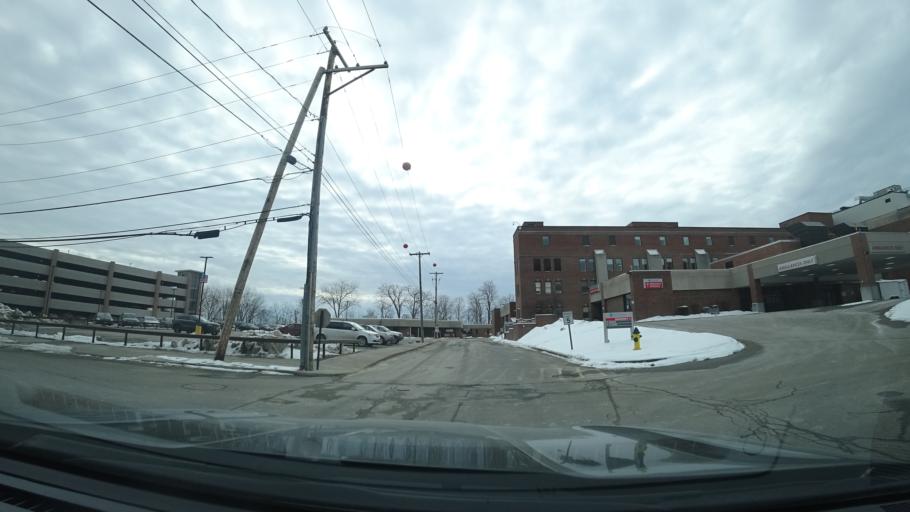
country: US
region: New York
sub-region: Warren County
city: Glens Falls
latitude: 43.3075
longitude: -73.6460
